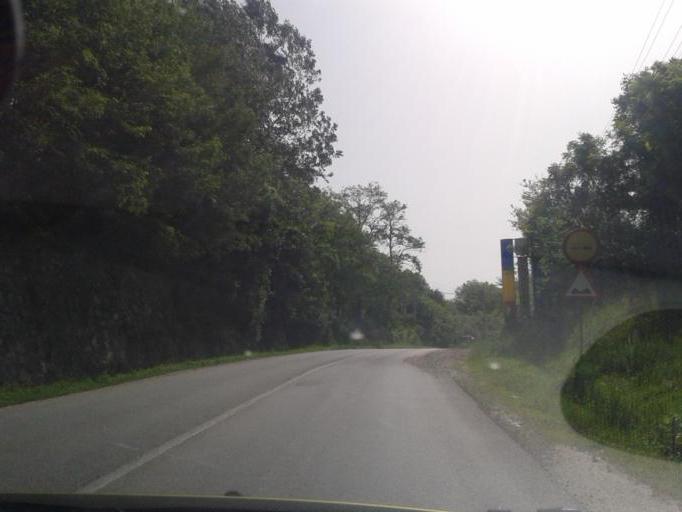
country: RO
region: Valcea
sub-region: Comuna Costesti
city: Costesti
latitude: 45.1417
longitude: 24.0742
